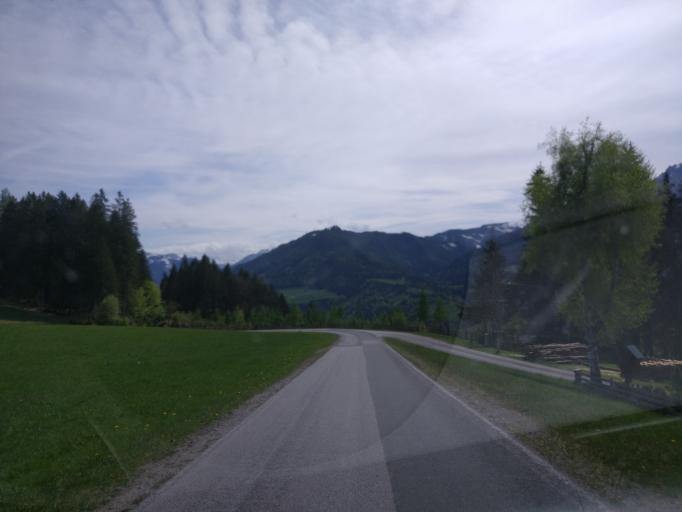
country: AT
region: Salzburg
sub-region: Politischer Bezirk Sankt Johann im Pongau
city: Pfarrwerfen
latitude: 47.4768
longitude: 13.2057
